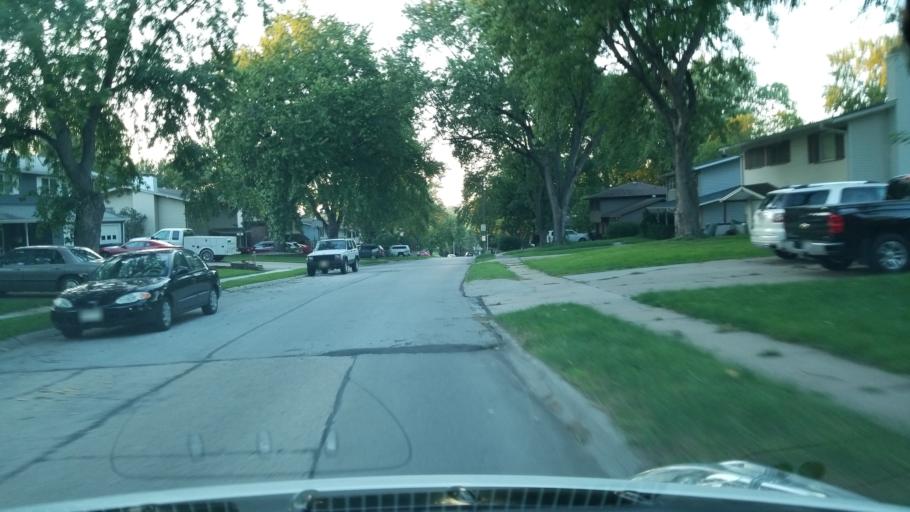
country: US
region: Nebraska
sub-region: Sarpy County
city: Bellevue
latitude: 41.1491
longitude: -95.9111
